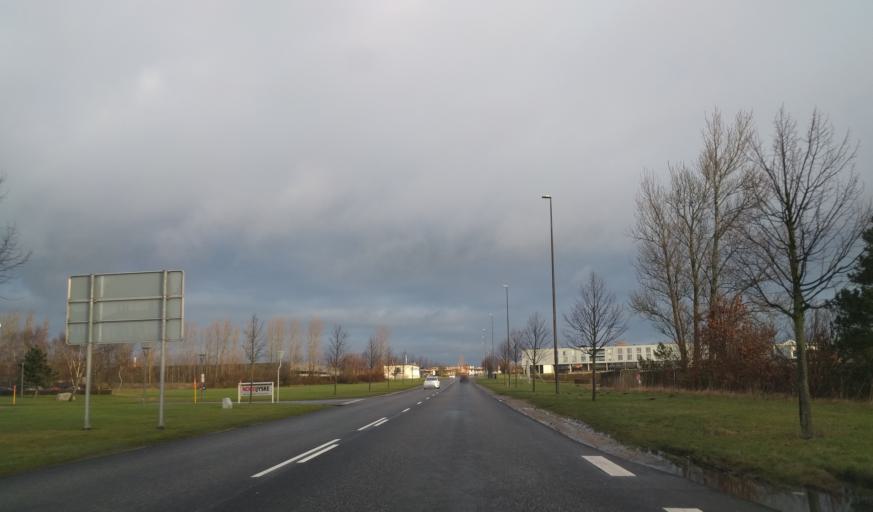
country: DK
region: North Denmark
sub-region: Alborg Kommune
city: Gistrup
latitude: 57.0208
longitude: 9.9758
